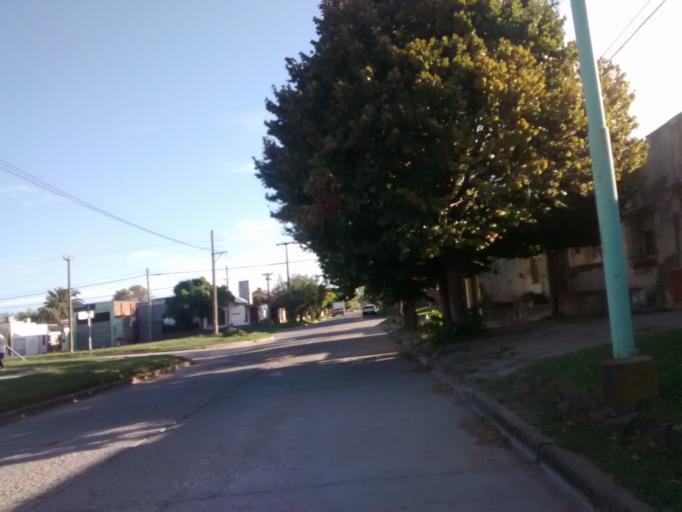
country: AR
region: Buenos Aires
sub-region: Partido de Loberia
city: Loberia
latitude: -38.1685
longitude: -58.7799
